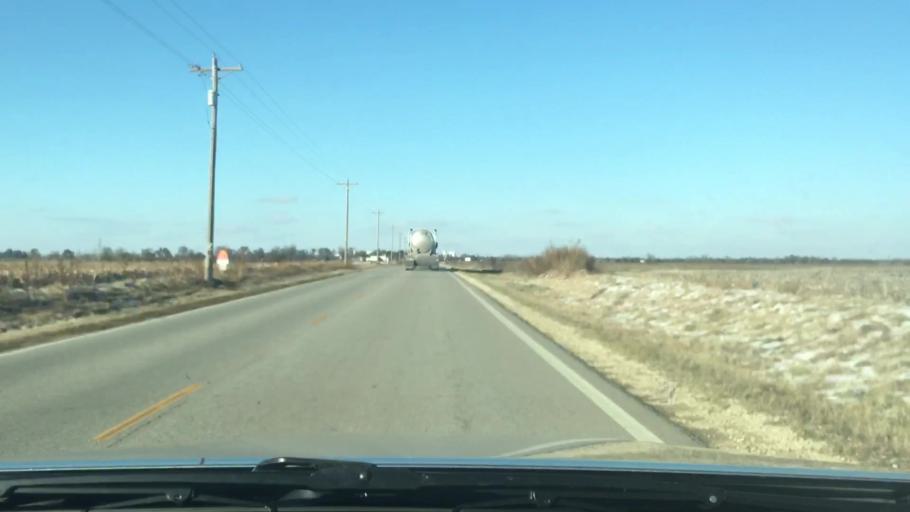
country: US
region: Kansas
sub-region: Rice County
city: Sterling
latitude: 38.1780
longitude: -98.2069
